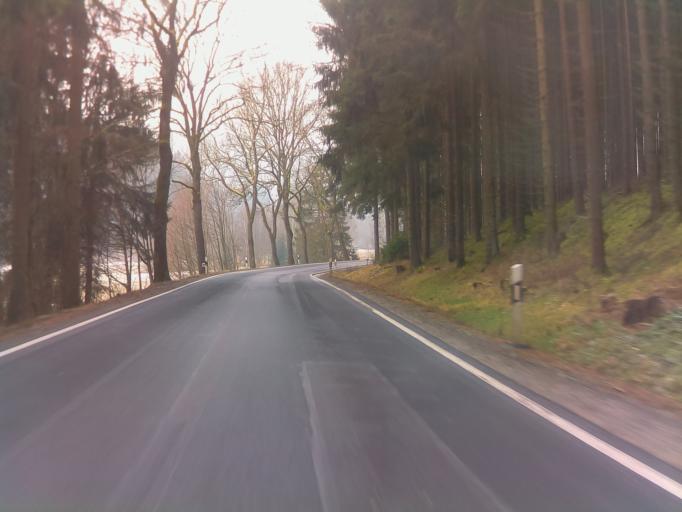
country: DE
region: Thuringia
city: Viernau
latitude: 50.6397
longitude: 10.5503
